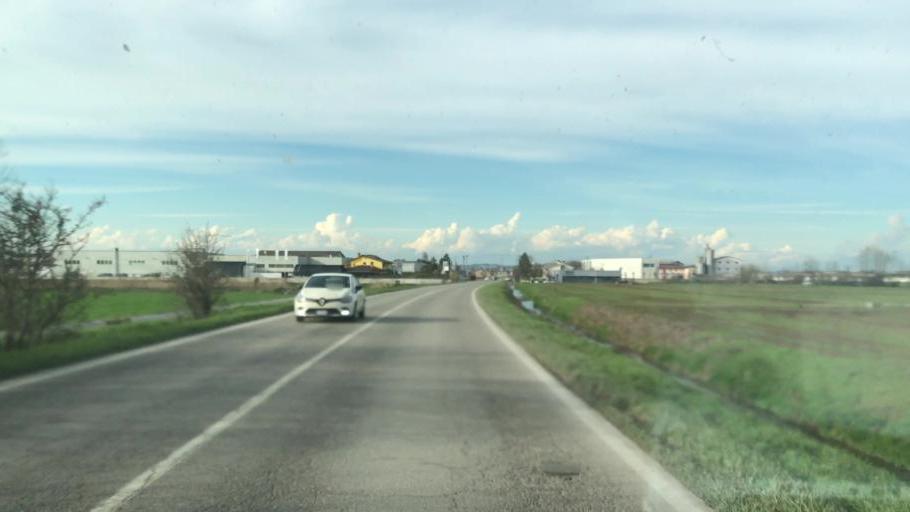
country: IT
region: Lombardy
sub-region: Provincia di Mantova
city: Cerlongo
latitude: 45.2720
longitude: 10.6606
